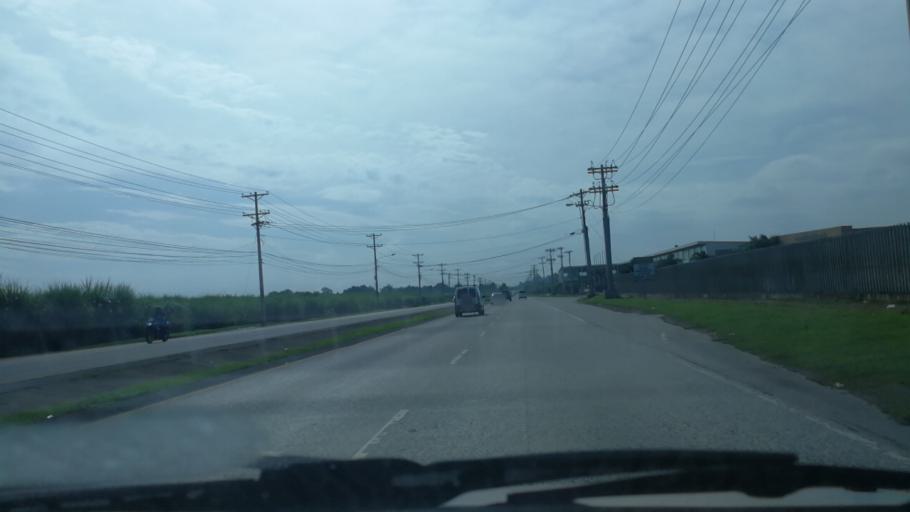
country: PA
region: Panama
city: Cabra Numero Uno
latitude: 9.0990
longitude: -79.3117
